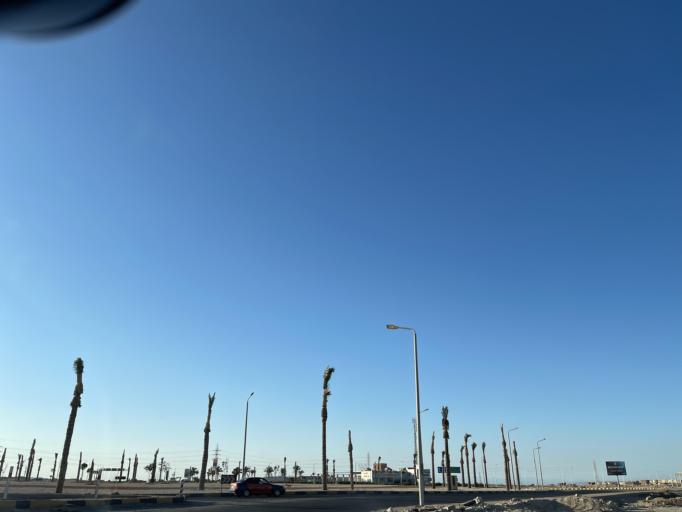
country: EG
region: Red Sea
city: Hurghada
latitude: 27.2301
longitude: 33.7813
